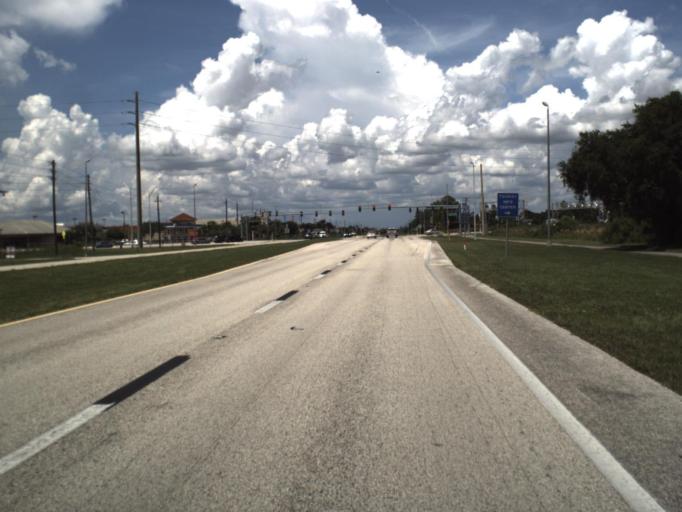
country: US
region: Florida
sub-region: Charlotte County
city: Charlotte Park
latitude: 26.8897
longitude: -82.0218
